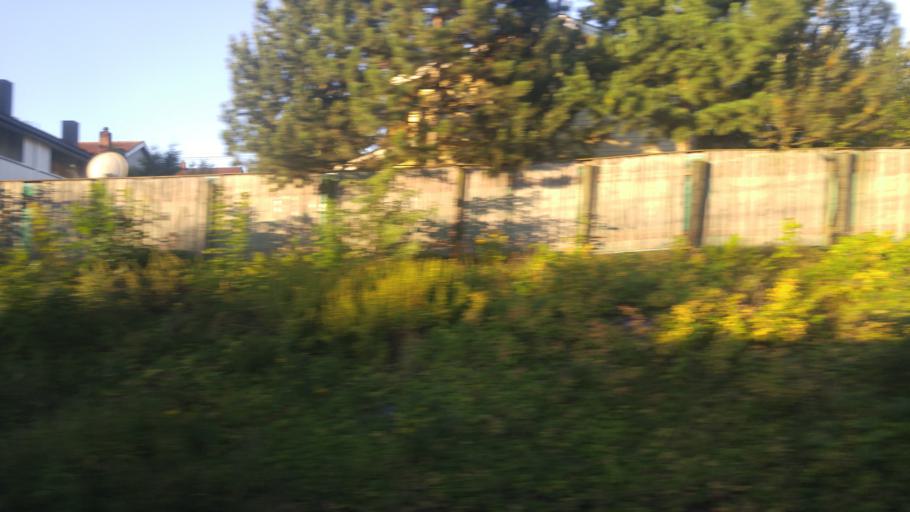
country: NO
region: Akershus
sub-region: Lorenskog
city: Kjenn
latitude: 59.9490
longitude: 10.9157
